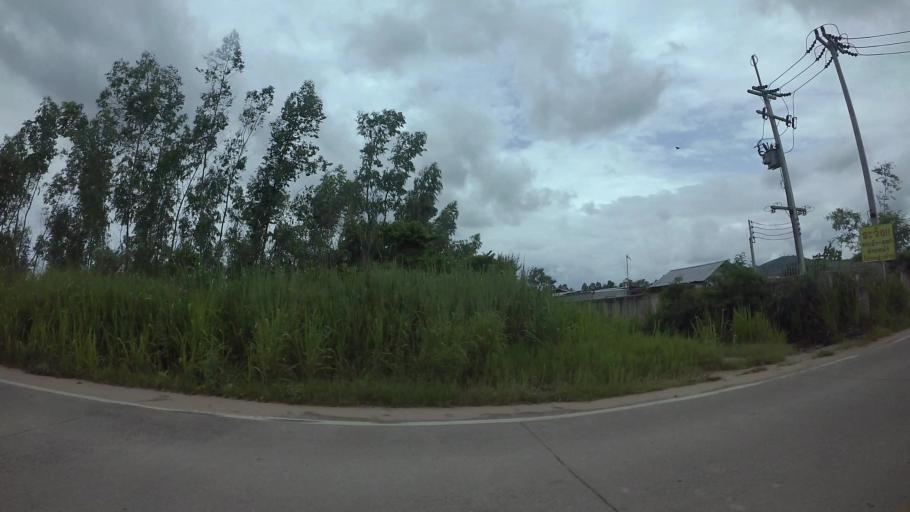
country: TH
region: Chon Buri
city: Si Racha
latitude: 13.1755
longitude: 100.9827
